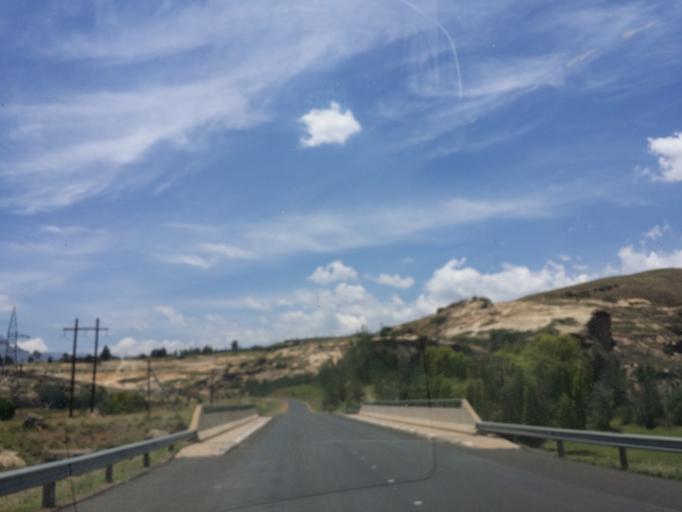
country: LS
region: Butha-Buthe
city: Butha-Buthe
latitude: -28.7367
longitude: 28.4186
